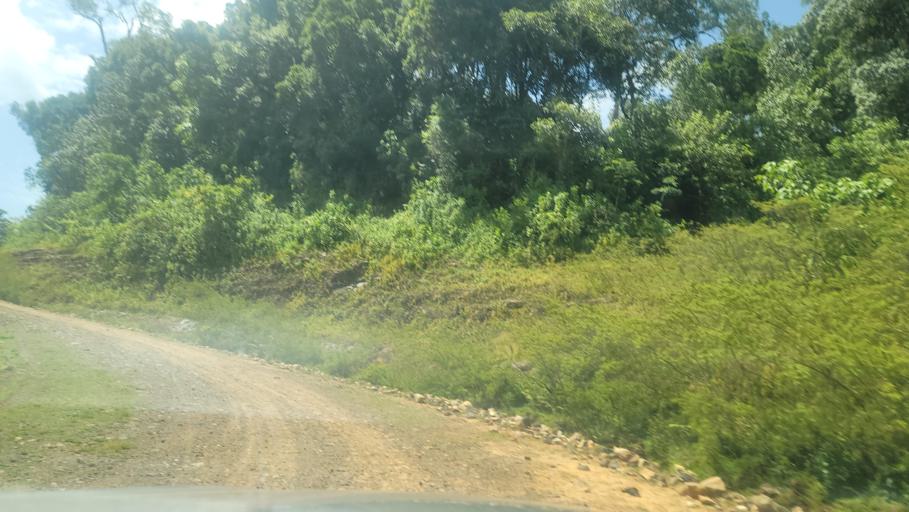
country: ET
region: Southern Nations, Nationalities, and People's Region
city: Bonga
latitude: 7.6813
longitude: 36.2404
